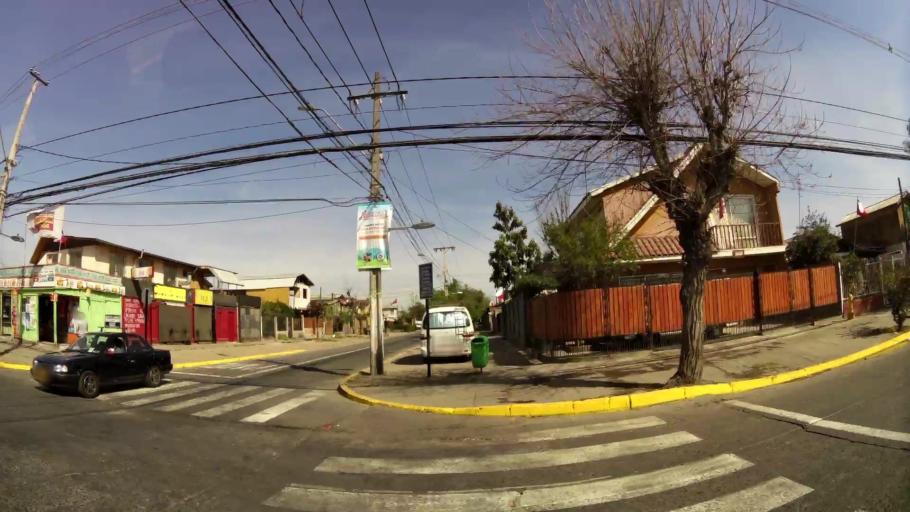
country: CL
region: Santiago Metropolitan
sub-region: Provincia de Santiago
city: La Pintana
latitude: -33.5356
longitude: -70.6014
